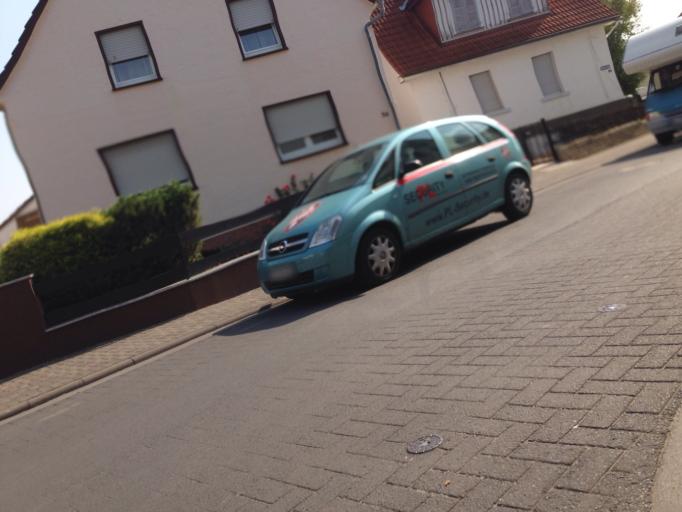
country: DE
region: Hesse
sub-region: Regierungsbezirk Giessen
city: Giessen
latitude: 50.6058
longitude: 8.7106
